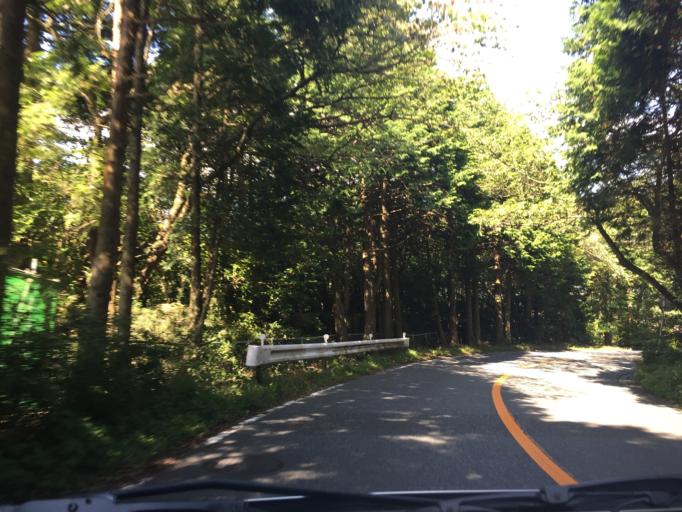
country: JP
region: Kanagawa
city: Hakone
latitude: 35.2548
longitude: 138.9994
